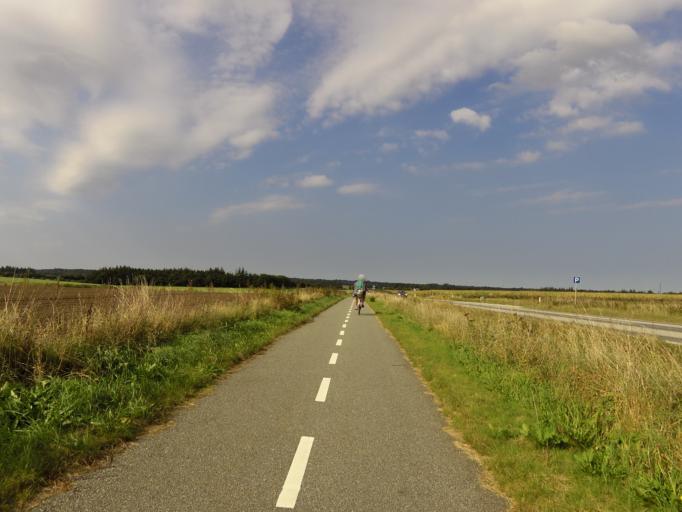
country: DK
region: South Denmark
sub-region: Vejen Kommune
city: Vejen
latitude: 55.4337
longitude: 9.1422
